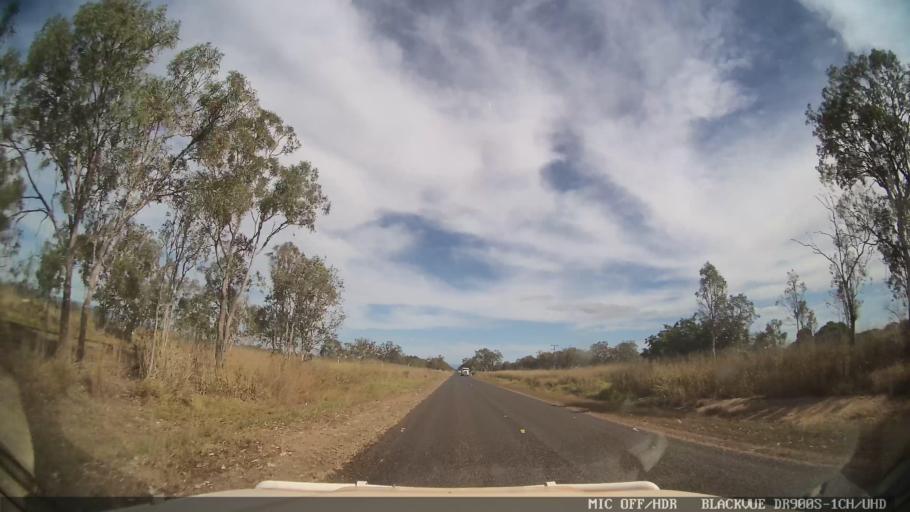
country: AU
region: Queensland
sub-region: Tablelands
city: Mareeba
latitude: -16.9376
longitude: 145.4170
